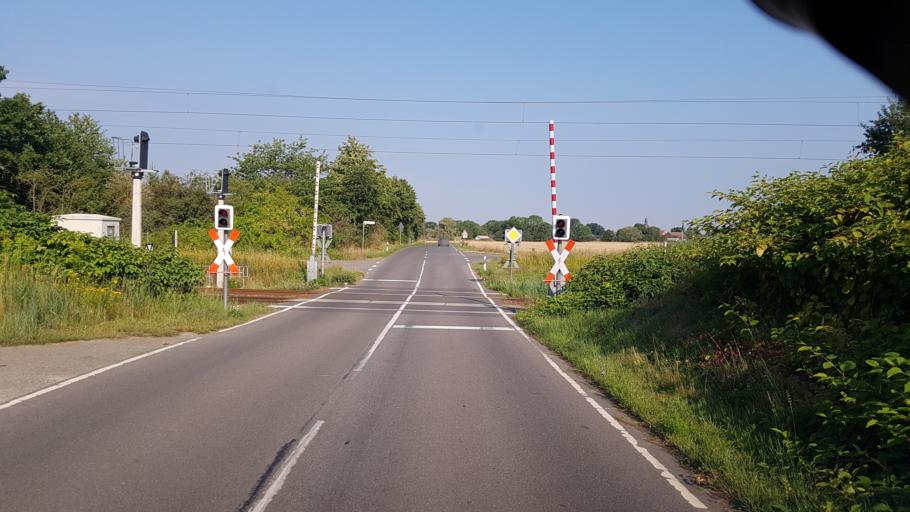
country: DE
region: Brandenburg
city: Drebkau
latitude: 51.6674
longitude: 14.2401
